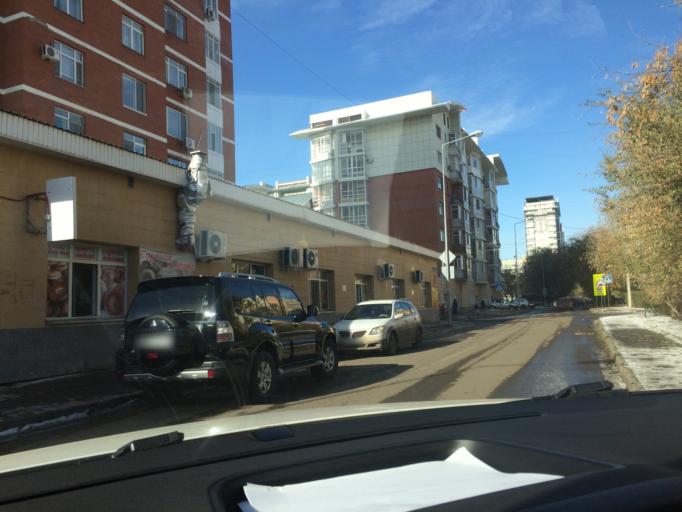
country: KZ
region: Astana Qalasy
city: Astana
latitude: 51.1582
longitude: 71.4336
